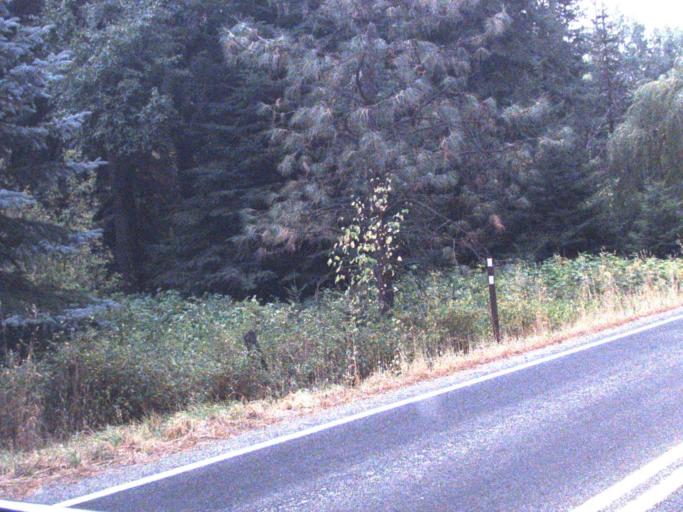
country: US
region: Washington
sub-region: Spokane County
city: Trentwood
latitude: 47.8358
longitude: -117.1944
